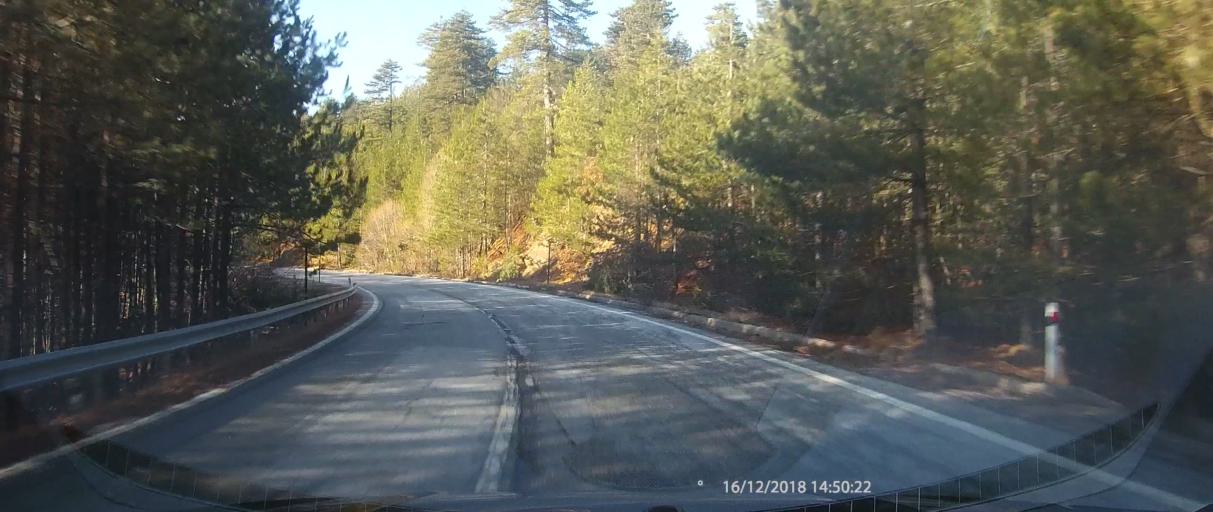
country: GR
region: West Macedonia
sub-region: Nomos Kastorias
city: Nestorio
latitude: 40.2076
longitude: 21.0808
